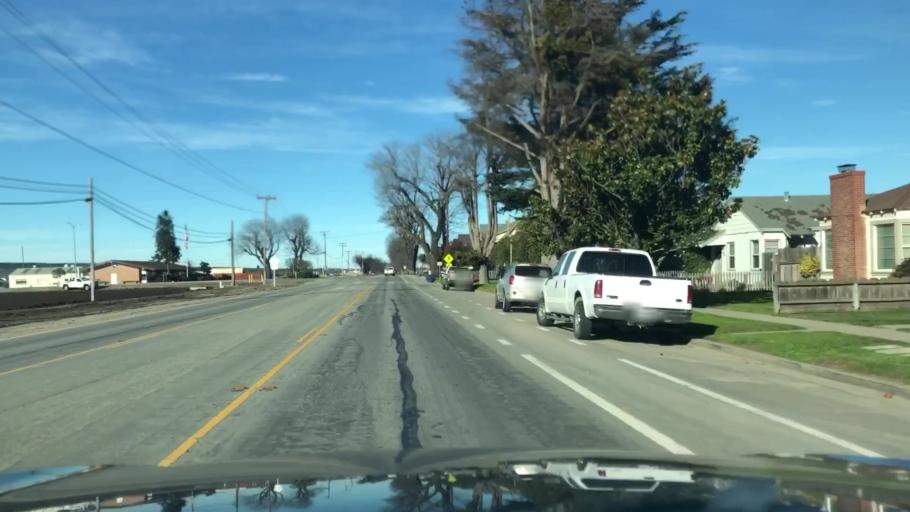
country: US
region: California
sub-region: Monterey County
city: Salinas
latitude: 36.6229
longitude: -121.6483
